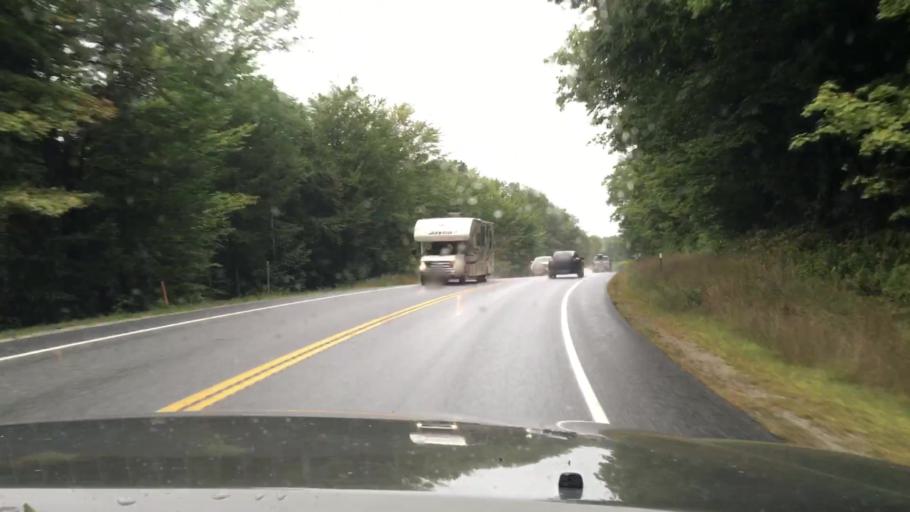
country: US
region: New Hampshire
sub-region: Hillsborough County
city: Antrim
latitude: 43.0664
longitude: -72.0582
